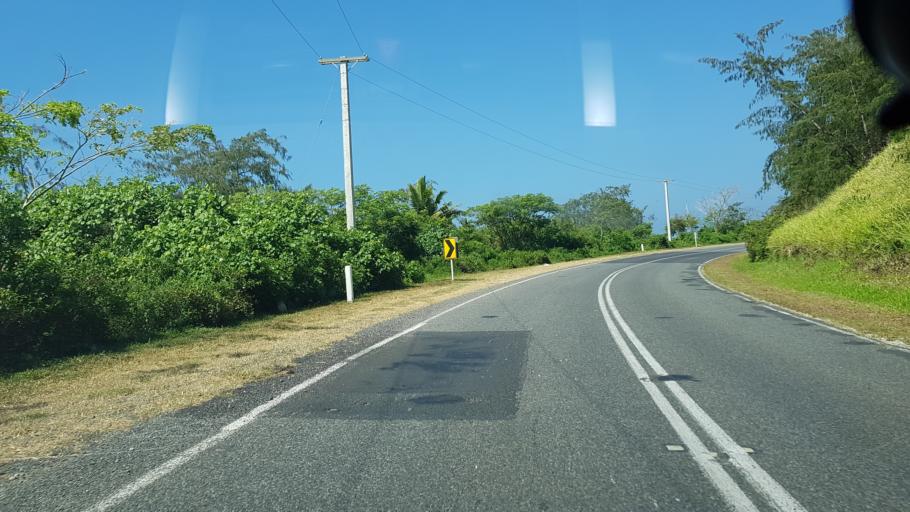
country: FJ
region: Western
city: Nadi
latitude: -18.1823
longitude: 177.5853
